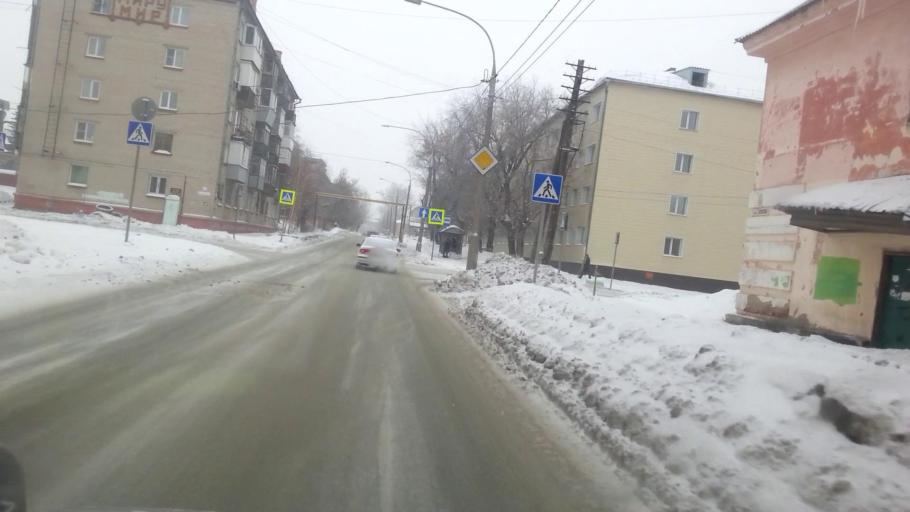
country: RU
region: Altai Krai
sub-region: Gorod Barnaulskiy
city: Barnaul
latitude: 53.3800
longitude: 83.7311
